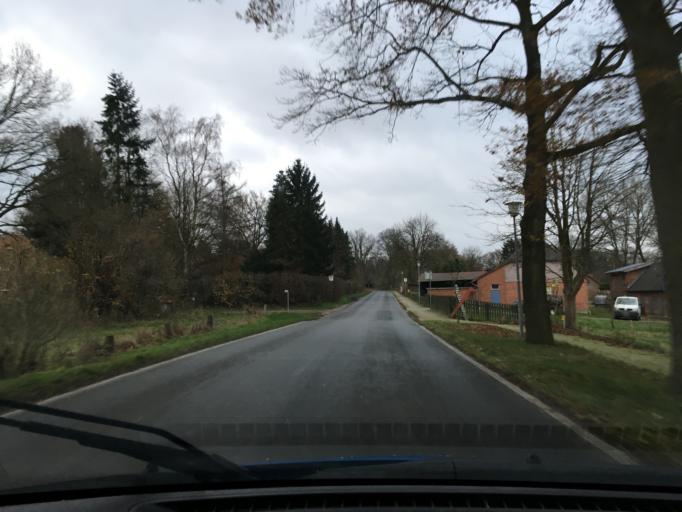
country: DE
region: Lower Saxony
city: Ebstorf
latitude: 53.0023
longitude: 10.4131
